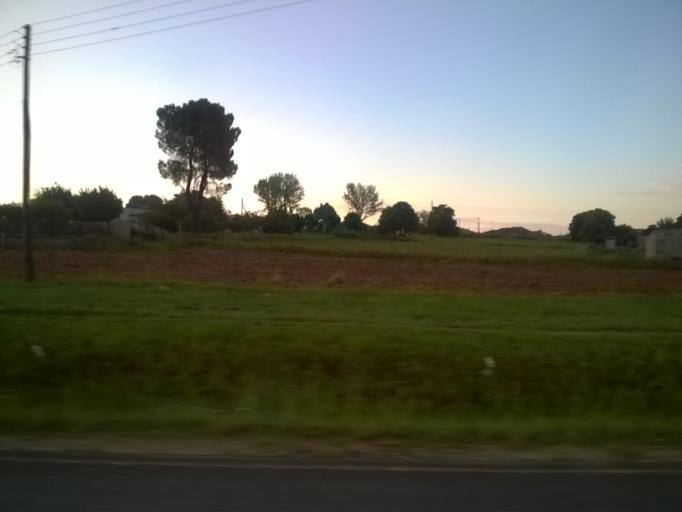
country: LS
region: Leribe
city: Leribe
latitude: -28.8705
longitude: 28.0570
